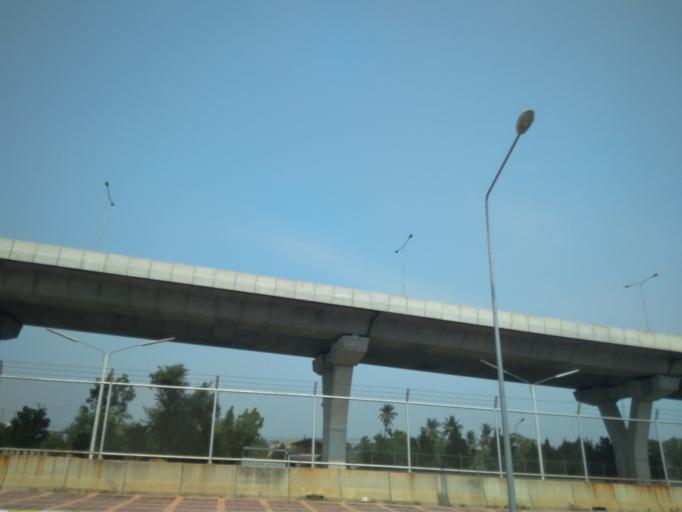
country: TH
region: Bangkok
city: Taling Chan
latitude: 13.7905
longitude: 100.4379
